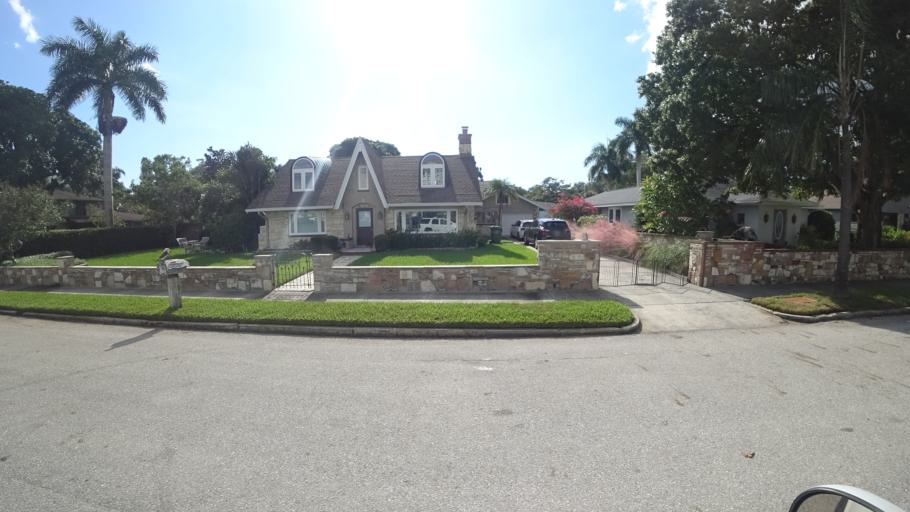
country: US
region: Florida
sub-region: Manatee County
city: Bradenton
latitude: 27.4973
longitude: -82.5811
